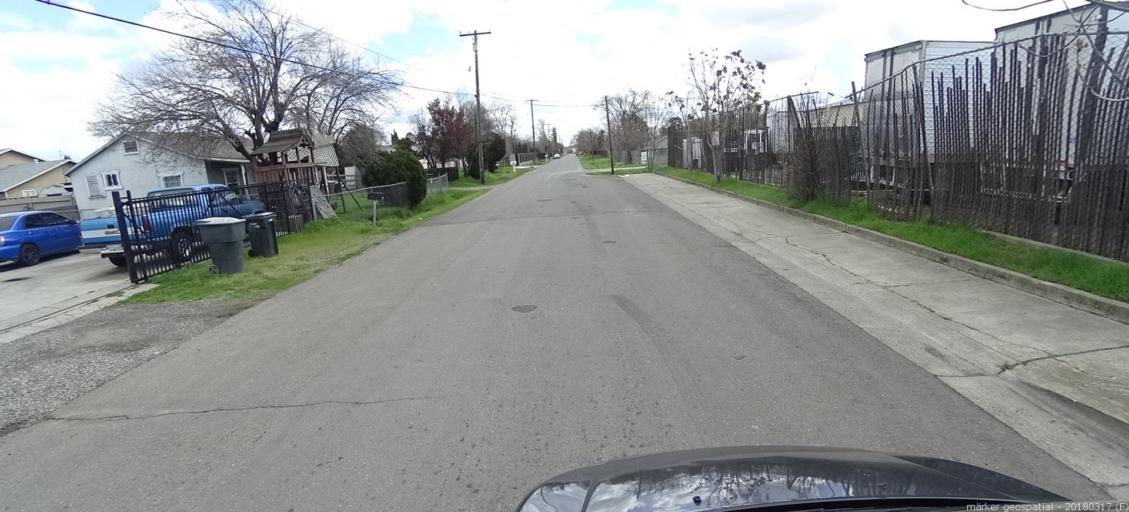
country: US
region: California
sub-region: Sacramento County
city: Florin
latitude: 38.4719
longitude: -121.4156
